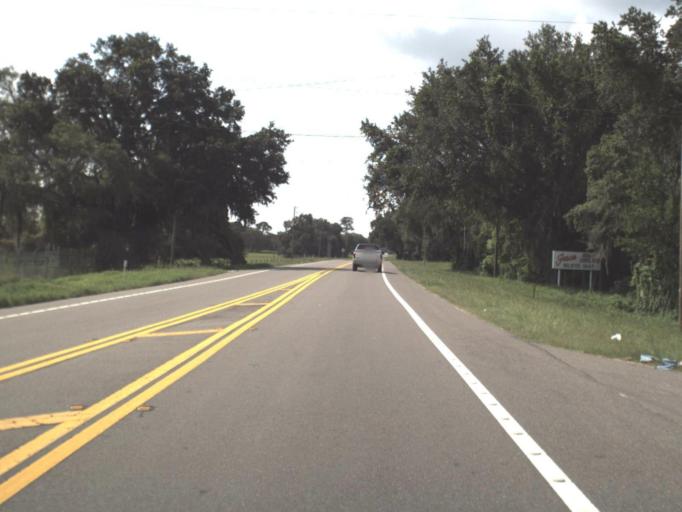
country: US
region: Florida
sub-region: Pasco County
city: Zephyrhills South
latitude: 28.2144
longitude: -82.1789
